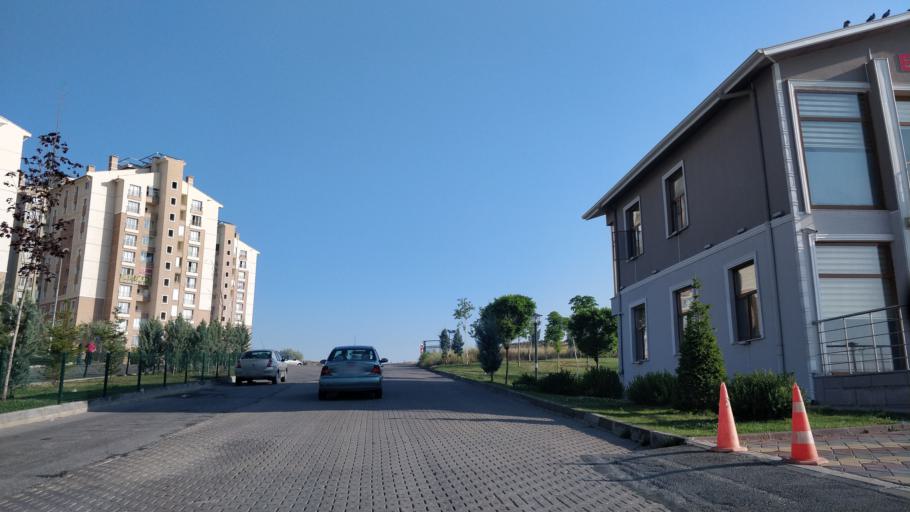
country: TR
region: Ankara
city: Etimesgut
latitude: 39.8438
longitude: 32.5464
